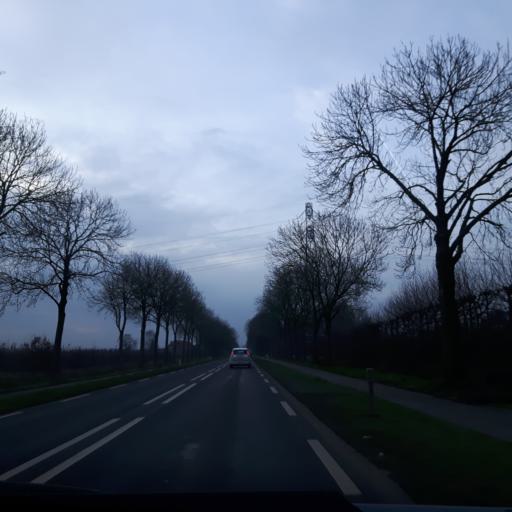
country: NL
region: Zeeland
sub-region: Gemeente Goes
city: Goes
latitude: 51.4745
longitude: 3.9033
